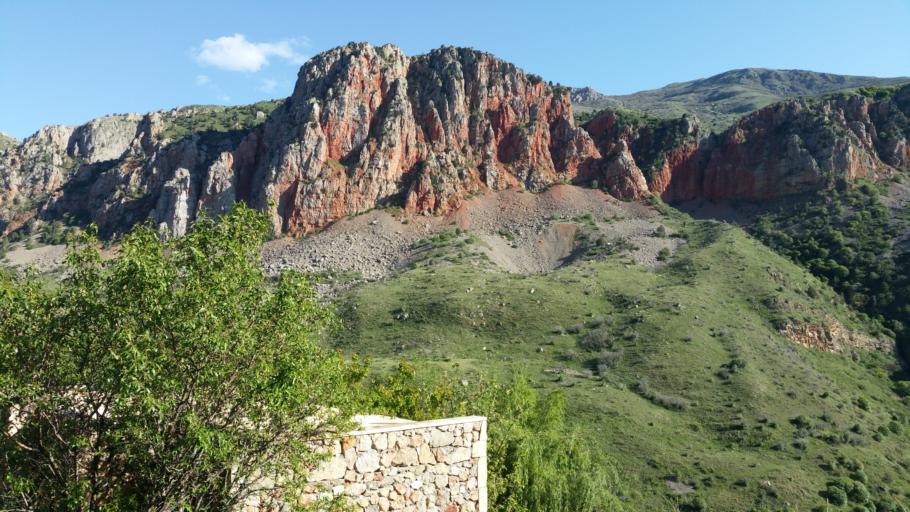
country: AM
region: Vayots' Dzori Marz
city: Areni
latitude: 39.6843
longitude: 45.2331
